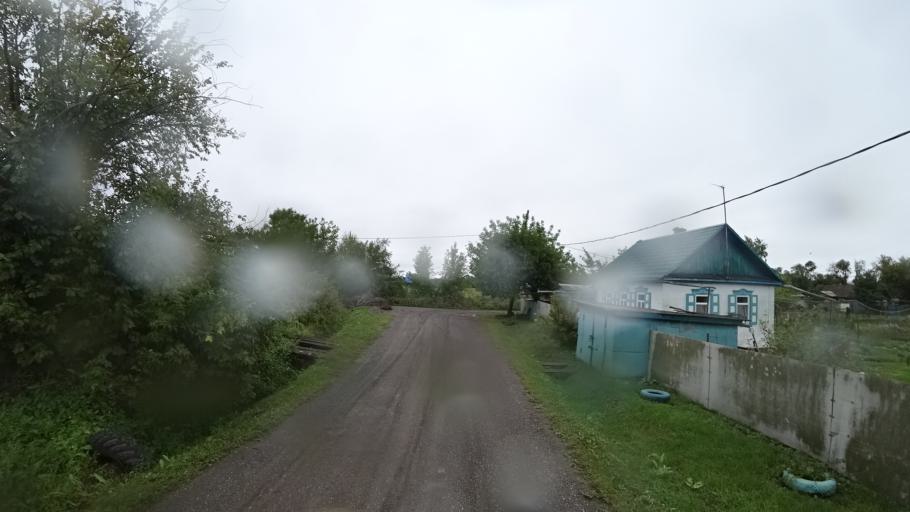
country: RU
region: Primorskiy
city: Monastyrishche
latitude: 44.2024
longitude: 132.4253
